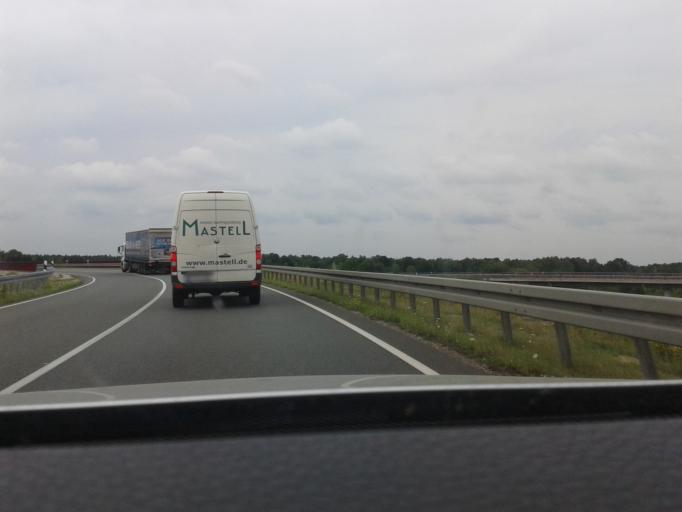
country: DE
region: Lower Saxony
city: Burgdorf
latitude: 52.4580
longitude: 9.9552
